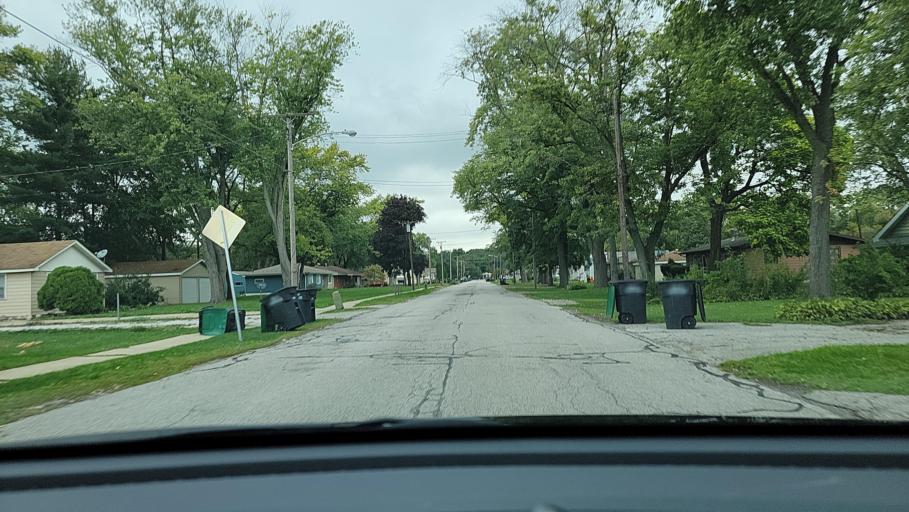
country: US
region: Indiana
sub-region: Porter County
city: Portage
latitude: 41.5616
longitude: -87.2059
